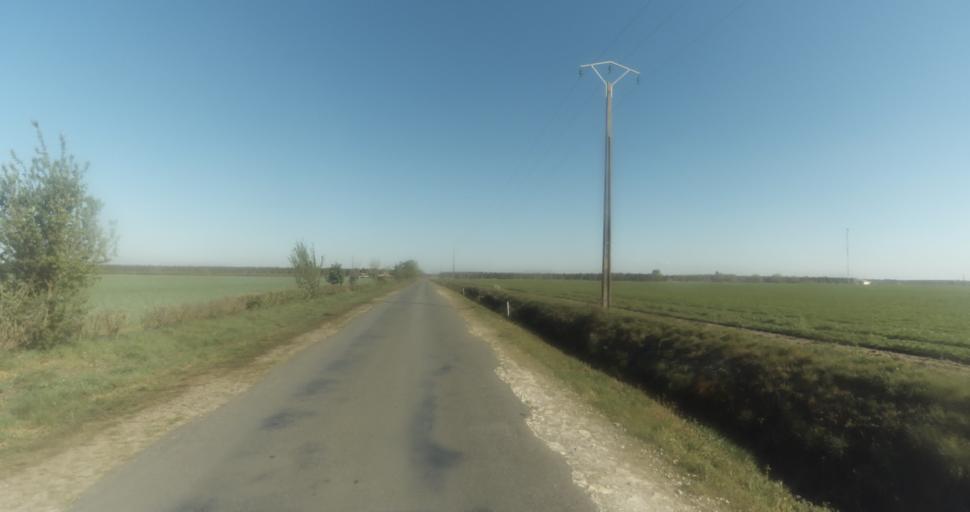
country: FR
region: Aquitaine
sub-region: Departement de la Gironde
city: Marcheprime
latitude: 44.7707
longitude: -0.8567
